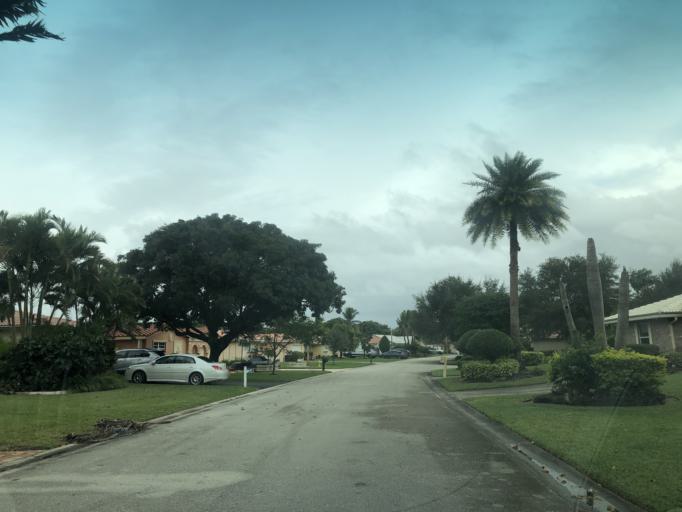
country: US
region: Florida
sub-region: Broward County
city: North Lauderdale
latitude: 26.2415
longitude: -80.2393
